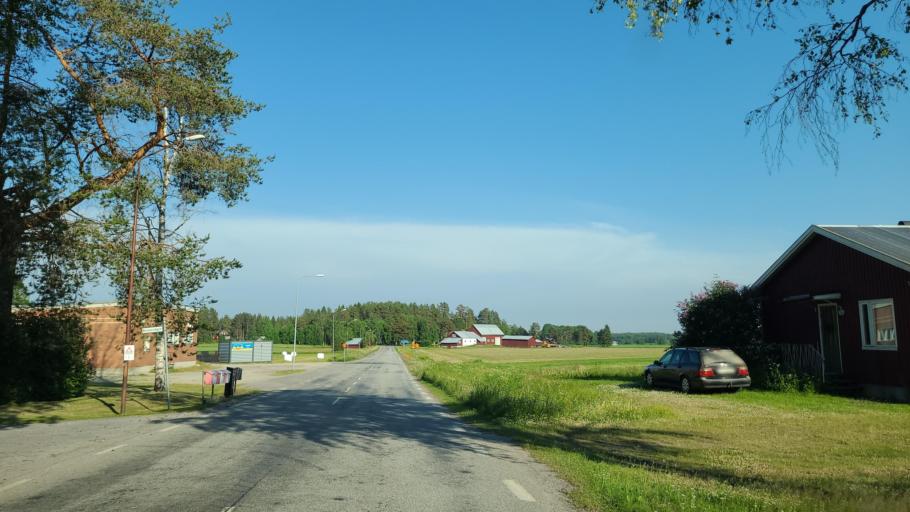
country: SE
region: Vaesterbotten
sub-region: Robertsfors Kommun
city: Robertsfors
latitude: 64.3019
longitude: 20.8714
